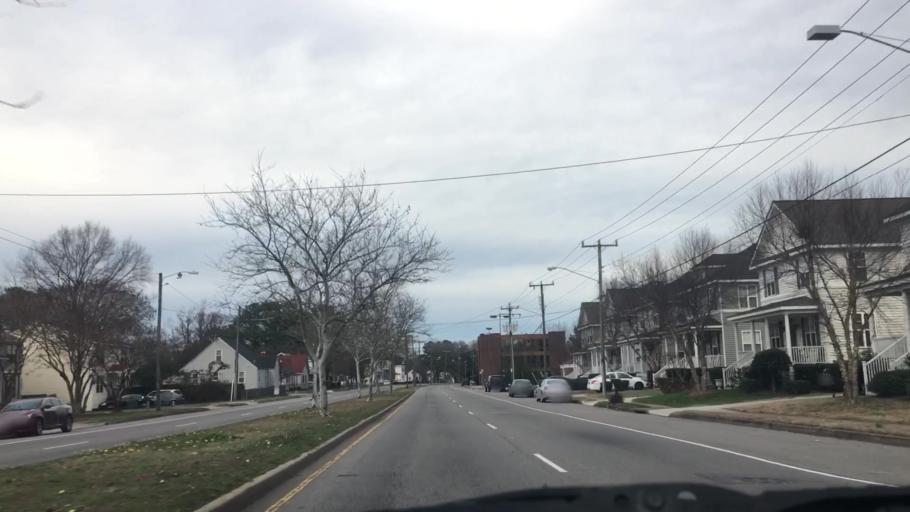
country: US
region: Virginia
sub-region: City of Norfolk
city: Norfolk
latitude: 36.8839
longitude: -76.2459
